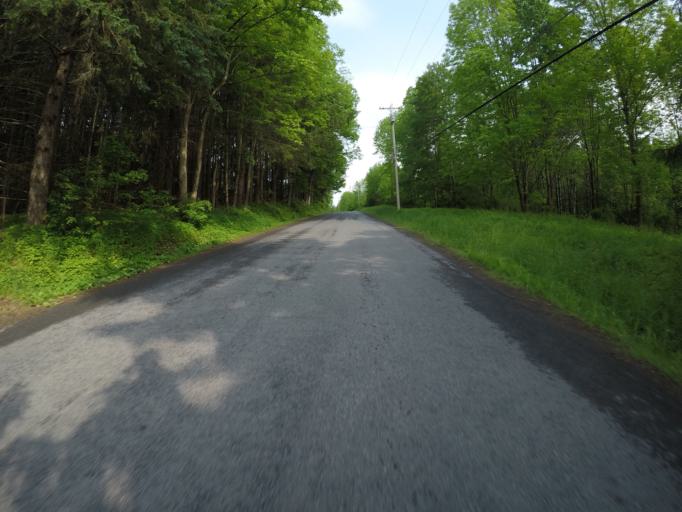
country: US
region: New York
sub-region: Delaware County
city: Stamford
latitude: 42.1570
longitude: -74.6556
